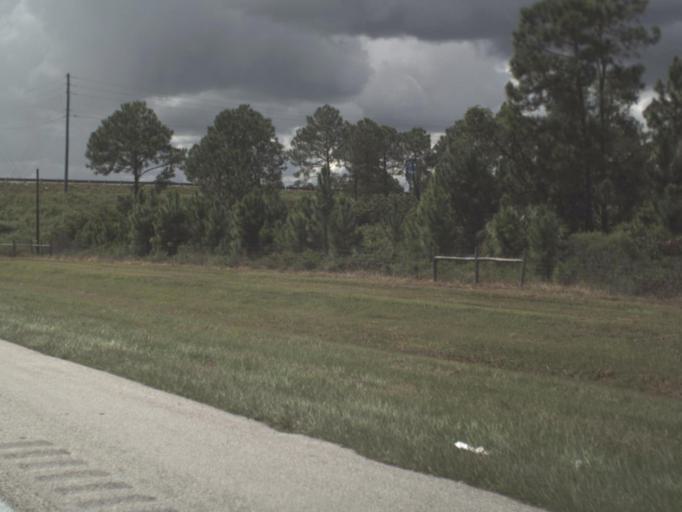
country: US
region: Florida
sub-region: Polk County
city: Polk City
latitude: 28.1827
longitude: -81.7429
